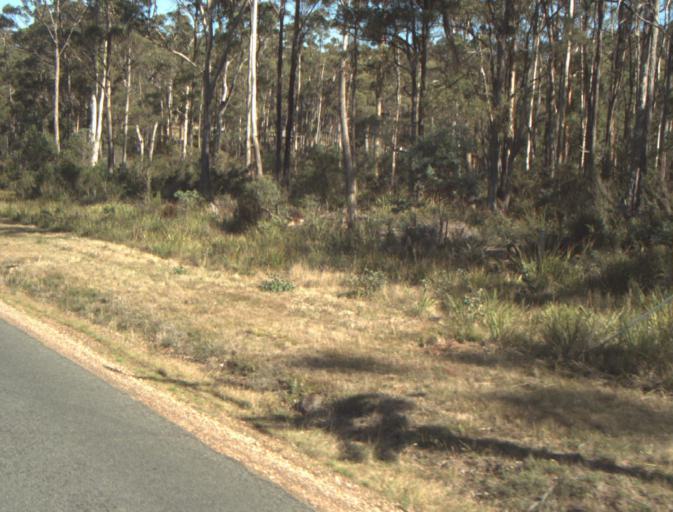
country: AU
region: Tasmania
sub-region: Launceston
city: Mayfield
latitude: -41.2908
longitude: 147.1296
